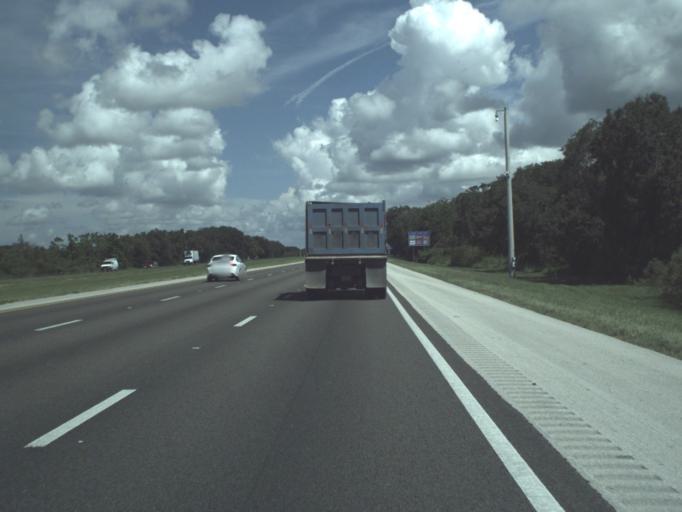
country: US
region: Florida
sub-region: Sarasota County
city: Lake Sarasota
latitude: 27.2574
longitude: -82.4489
